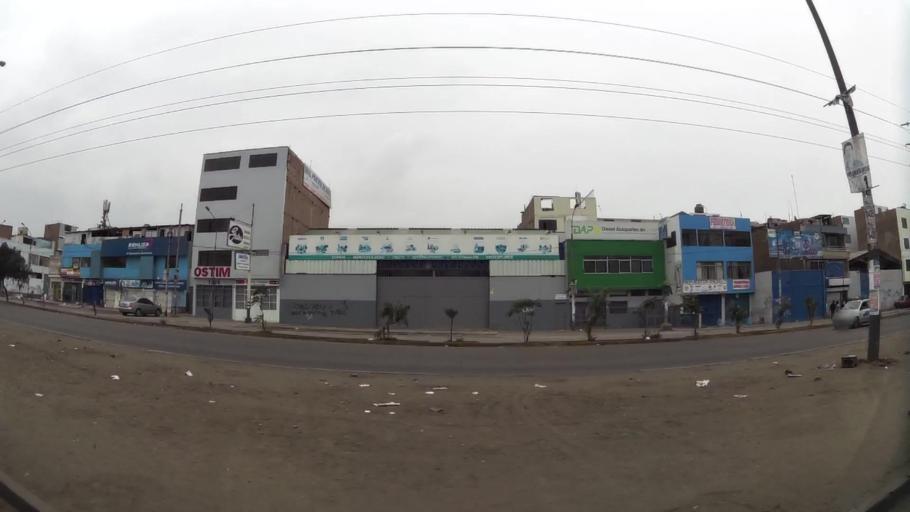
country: PE
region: Lima
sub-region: Lima
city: San Luis
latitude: -12.0739
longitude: -77.0063
